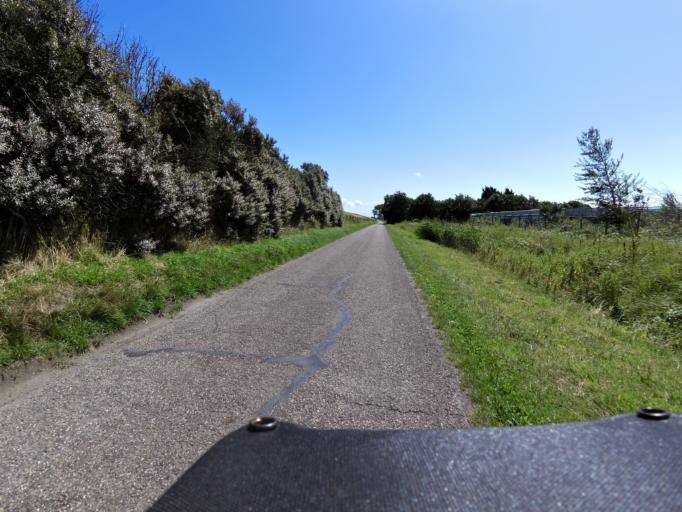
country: NL
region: South Holland
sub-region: Gemeente Goeree-Overflakkee
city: Goedereede
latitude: 51.8217
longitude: 4.0202
